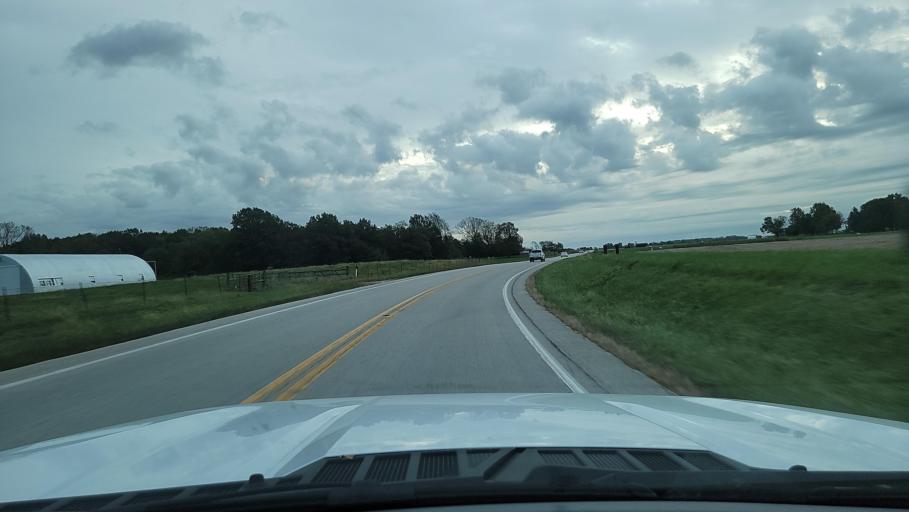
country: US
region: Illinois
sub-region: Schuyler County
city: Rushville
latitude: 40.1534
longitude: -90.5532
